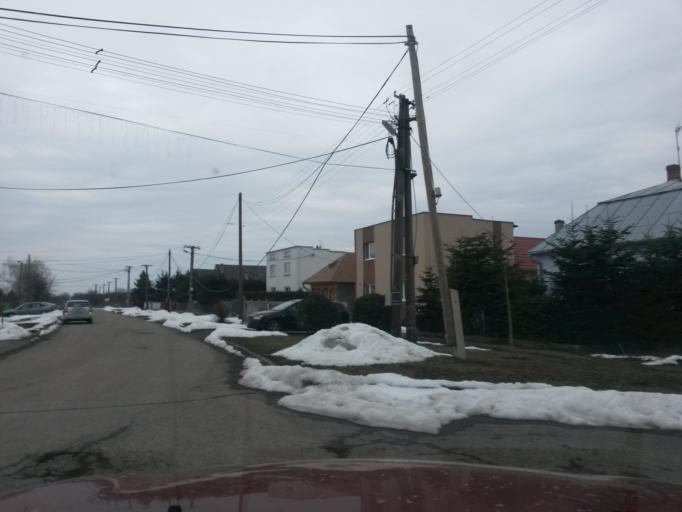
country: SK
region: Kosicky
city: Vinne
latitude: 48.7472
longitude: 22.0213
